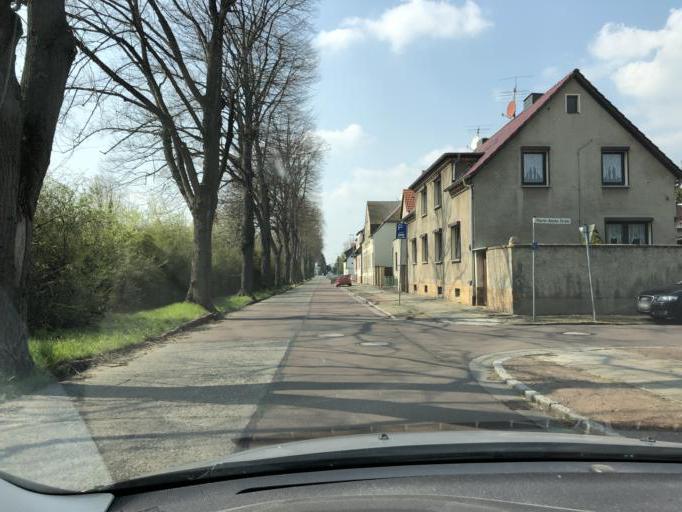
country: DE
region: Saxony-Anhalt
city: Zorbig
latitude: 51.6314
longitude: 12.1187
